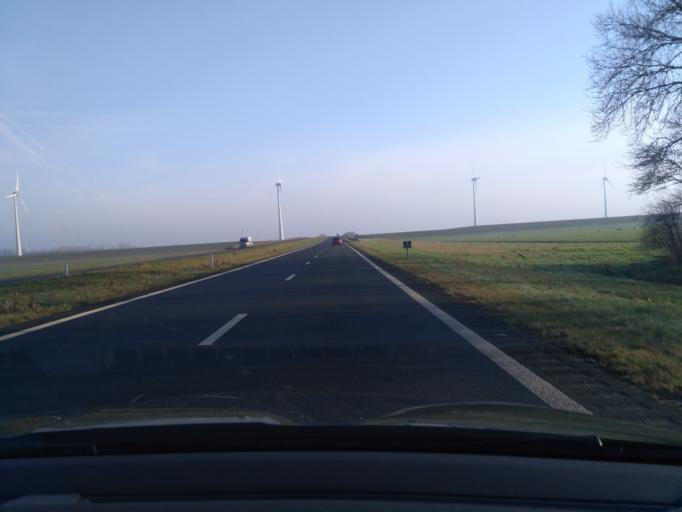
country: NL
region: Flevoland
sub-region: Gemeente Zeewolde
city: Zeewolde
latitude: 52.3744
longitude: 5.5427
